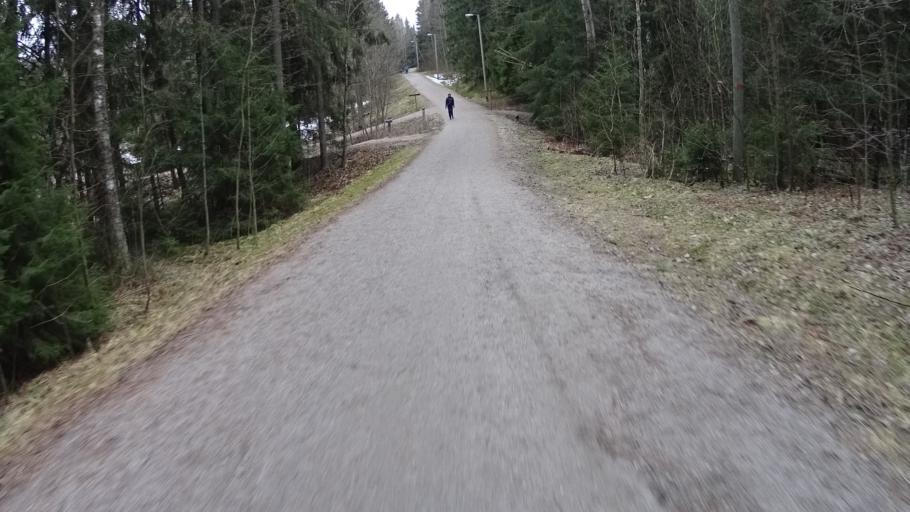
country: FI
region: Uusimaa
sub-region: Helsinki
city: Kauniainen
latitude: 60.1938
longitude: 24.6982
